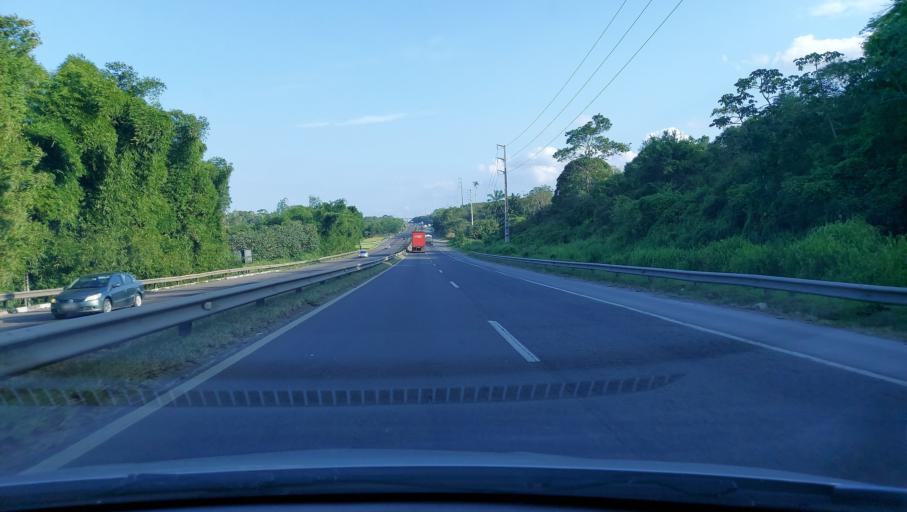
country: BR
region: Bahia
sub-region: Conceicao Do Jacuipe
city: Conceicao do Jacuipe
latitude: -12.3513
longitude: -38.8338
